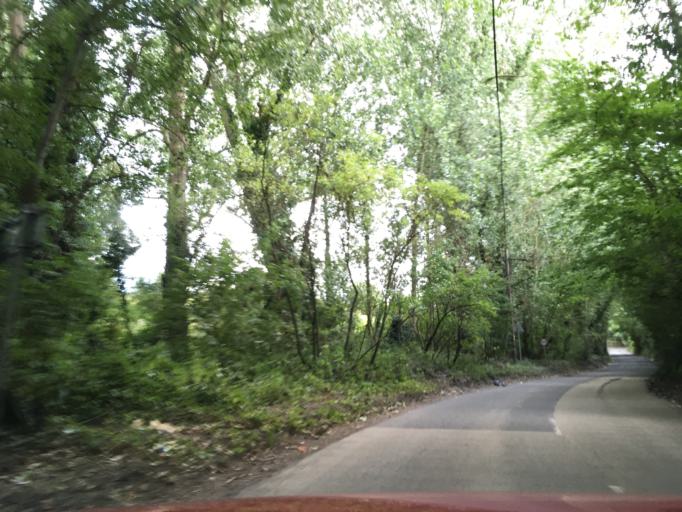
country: GB
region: England
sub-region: Kent
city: Wateringbury
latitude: 51.2449
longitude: 0.4531
